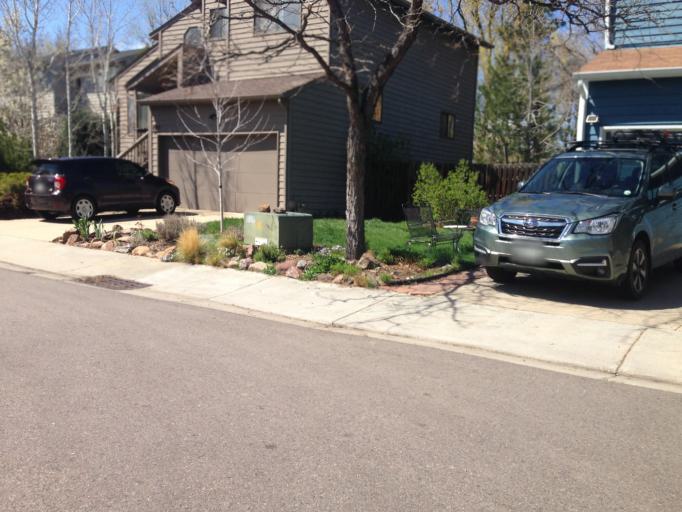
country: US
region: Colorado
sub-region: Boulder County
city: Boulder
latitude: 39.9882
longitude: -105.2220
